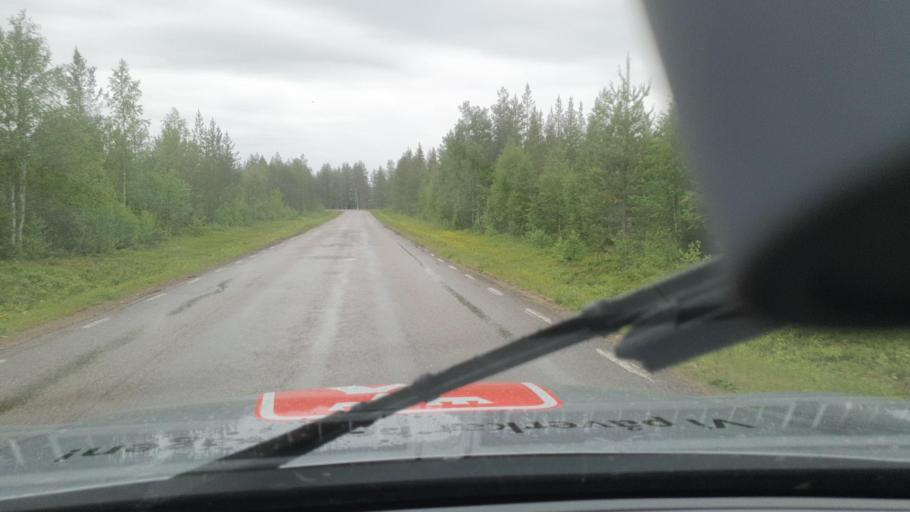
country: SE
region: Norrbotten
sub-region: Pajala Kommun
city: Pajala
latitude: 66.8222
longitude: 23.1174
